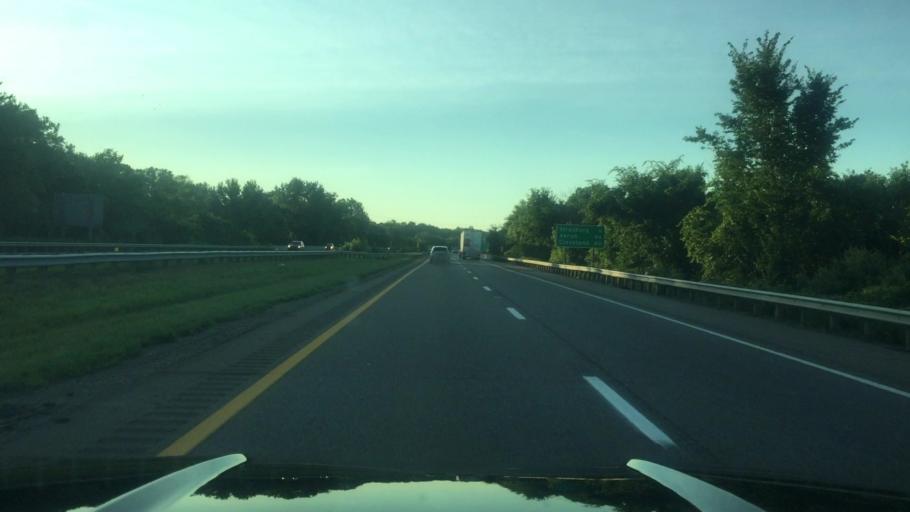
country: US
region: Ohio
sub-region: Tuscarawas County
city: Dover
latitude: 40.5099
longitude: -81.4845
